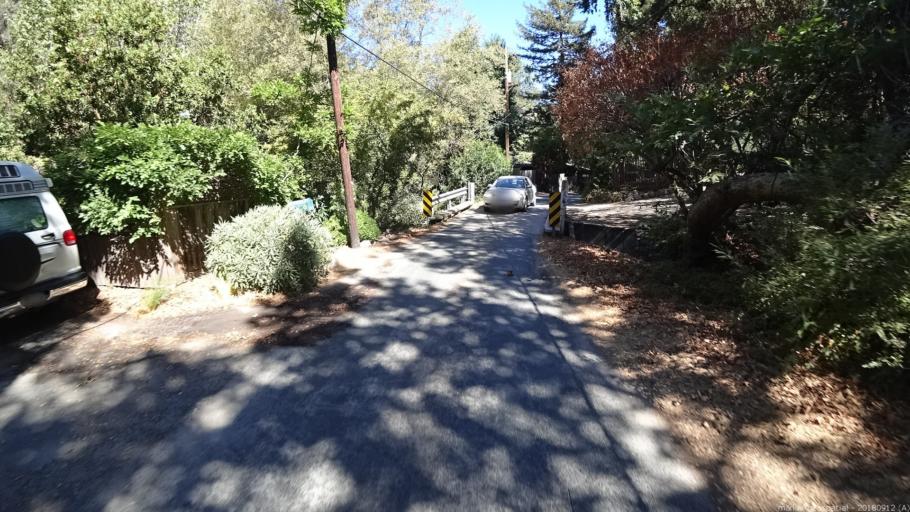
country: US
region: California
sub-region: Monterey County
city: Carmel Valley Village
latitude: 36.4650
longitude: -121.7242
